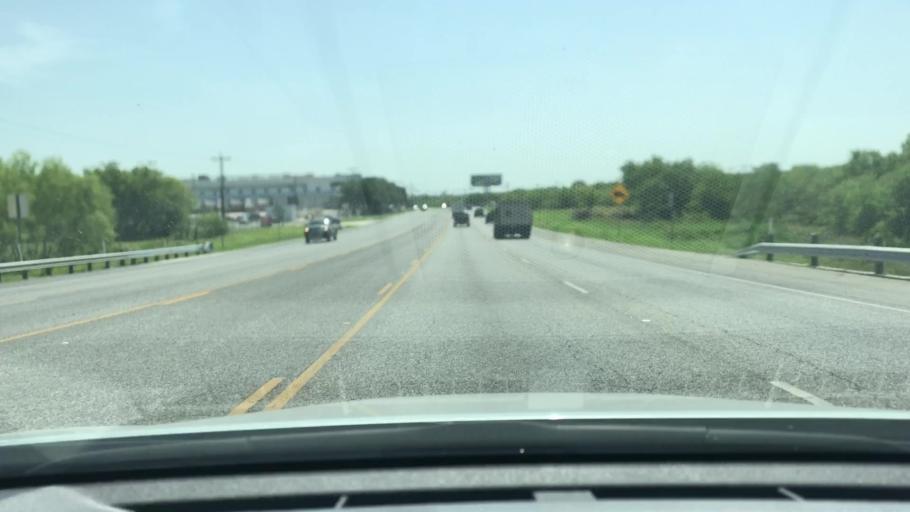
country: US
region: Texas
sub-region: Bexar County
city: Kirby
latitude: 29.4749
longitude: -98.3788
